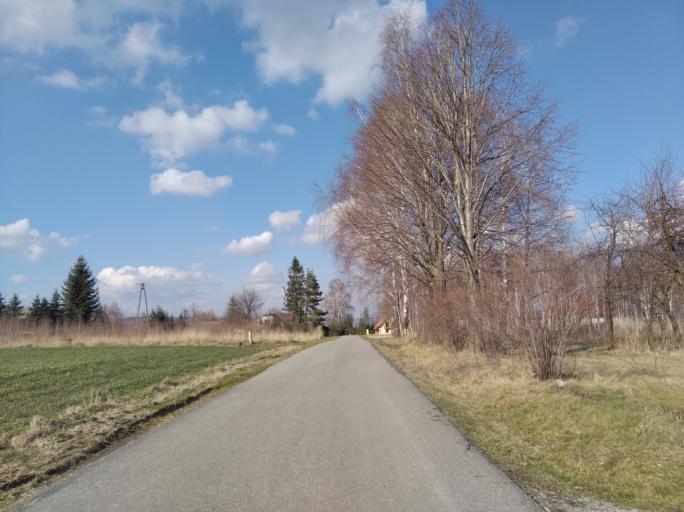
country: PL
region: Subcarpathian Voivodeship
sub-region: Powiat strzyzowski
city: Wysoka Strzyzowska
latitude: 49.8496
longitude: 21.7098
